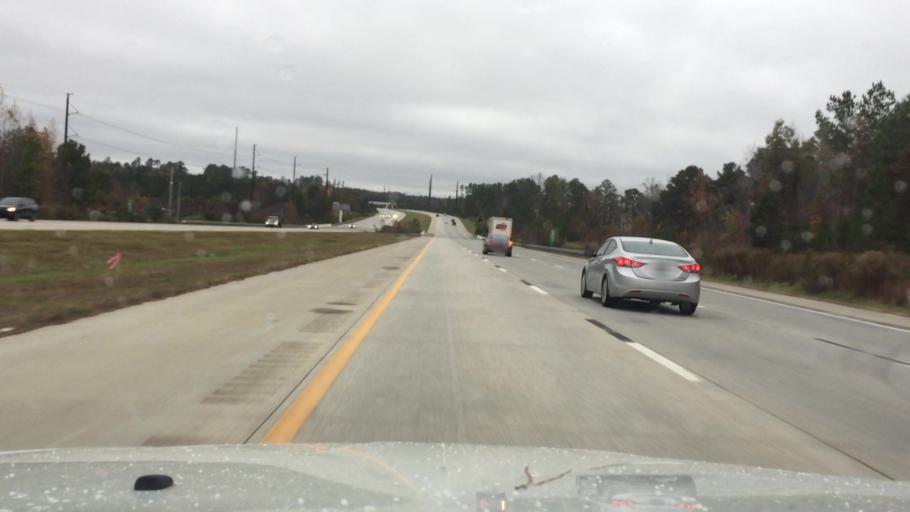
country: US
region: North Carolina
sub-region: Wake County
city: Green Level
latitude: 35.8125
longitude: -78.8921
